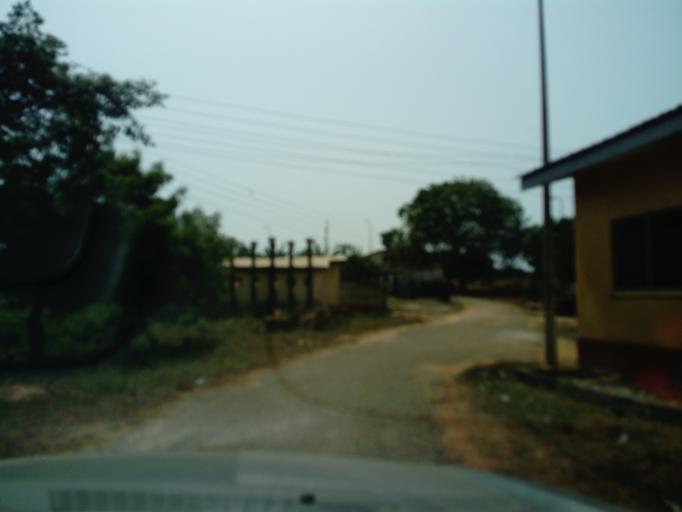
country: GH
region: Central
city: Cape Coast
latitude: 5.1057
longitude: -1.2751
